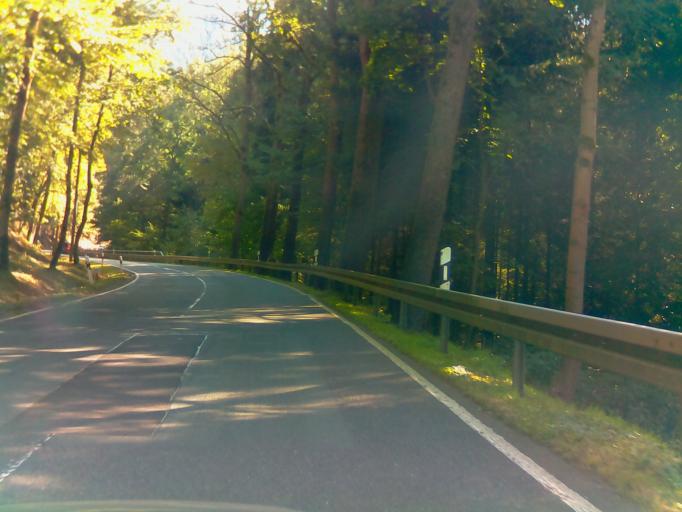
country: DE
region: Thuringia
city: Leutenberg
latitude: 50.5347
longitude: 11.4718
